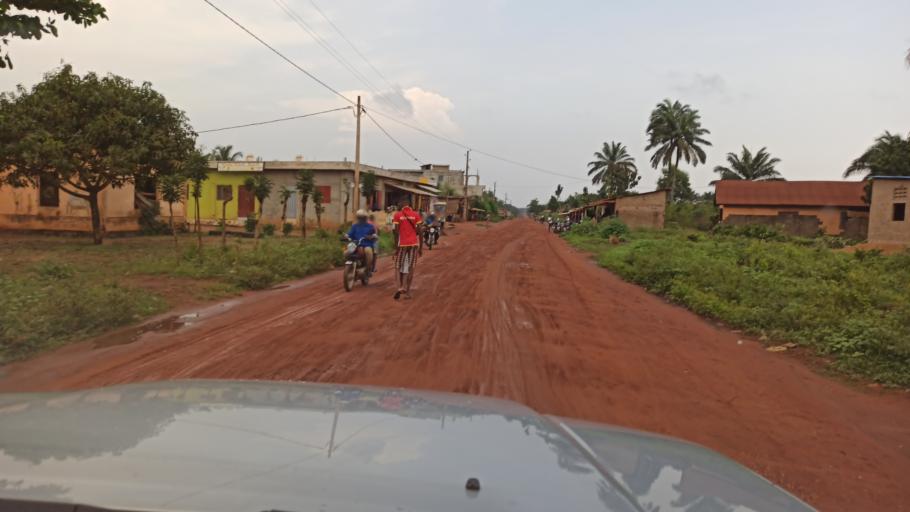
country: BJ
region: Queme
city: Porto-Novo
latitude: 6.4905
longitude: 2.6696
